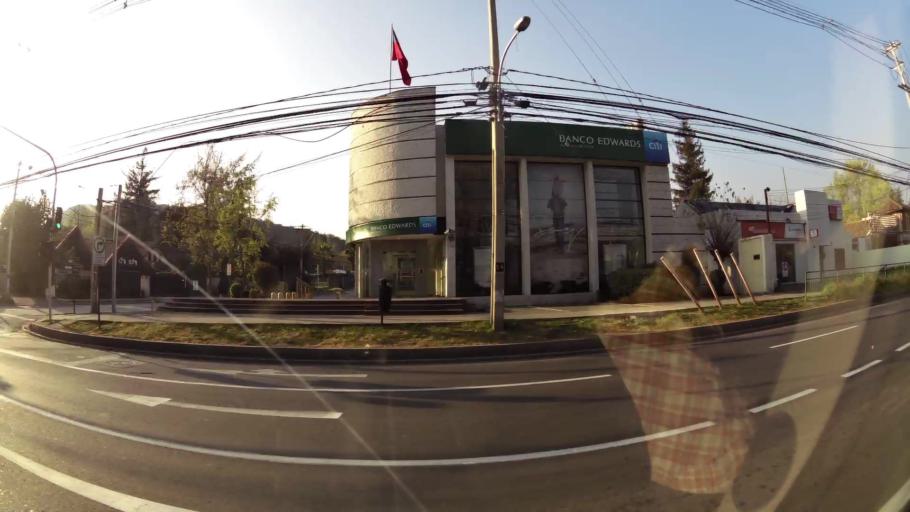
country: CL
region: Santiago Metropolitan
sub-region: Provincia de Santiago
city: Villa Presidente Frei, Nunoa, Santiago, Chile
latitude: -33.3533
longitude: -70.5226
